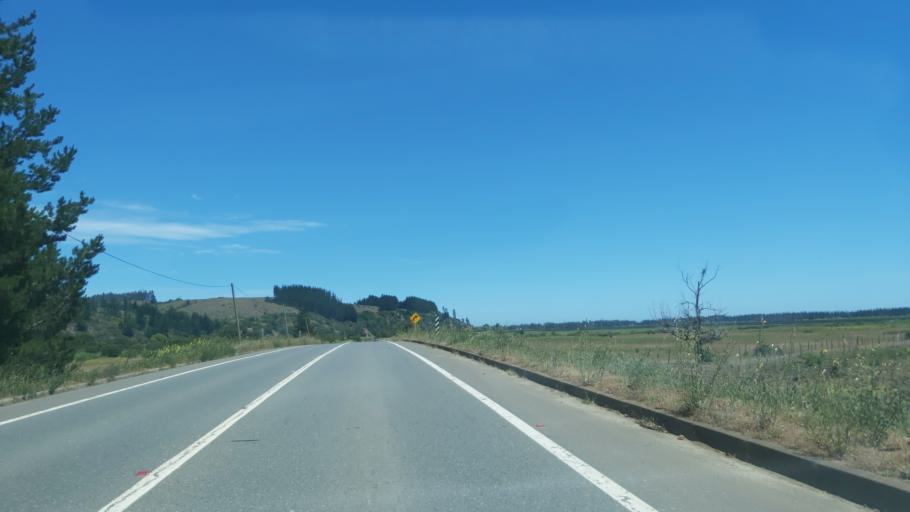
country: CL
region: Maule
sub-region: Provincia de Talca
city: Constitucion
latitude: -35.1545
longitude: -72.2263
